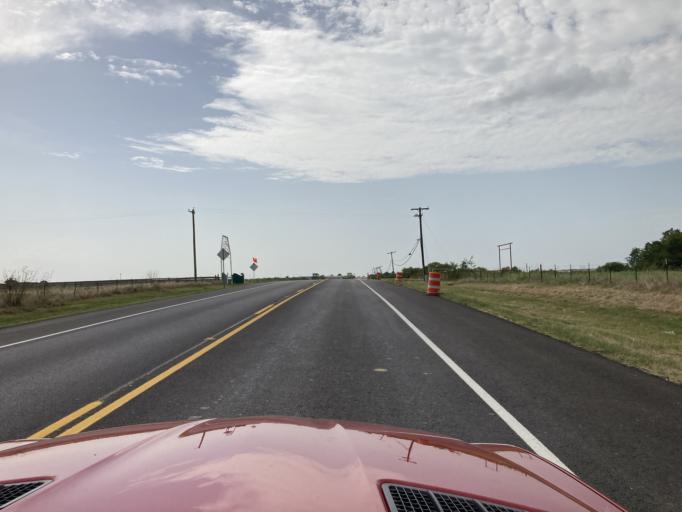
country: US
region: Texas
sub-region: Navarro County
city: Corsicana
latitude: 32.0552
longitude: -96.4266
